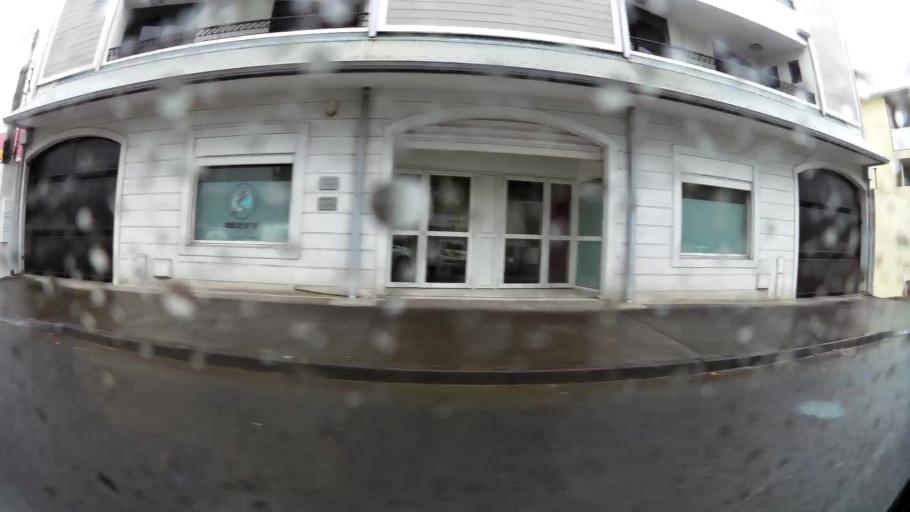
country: RE
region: Reunion
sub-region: Reunion
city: Saint-Andre
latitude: -20.9588
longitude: 55.6541
